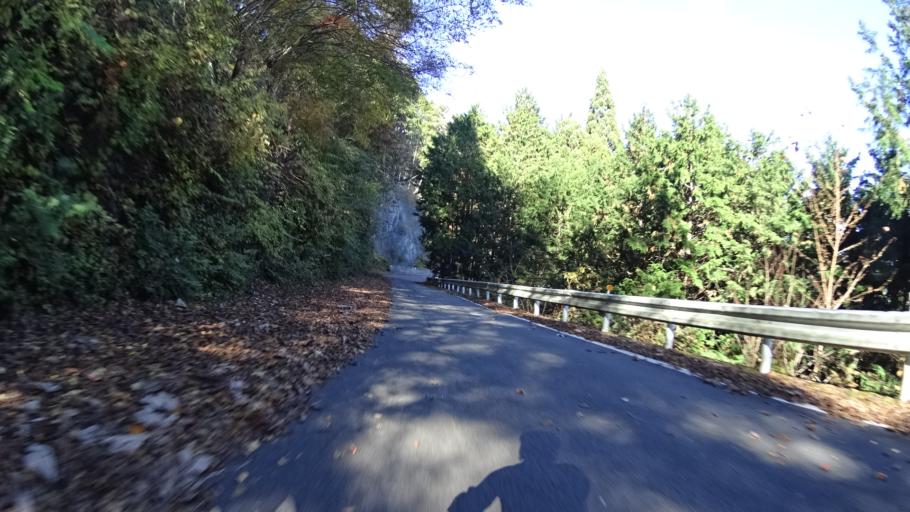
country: JP
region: Yamanashi
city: Otsuki
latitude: 35.7426
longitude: 138.9512
